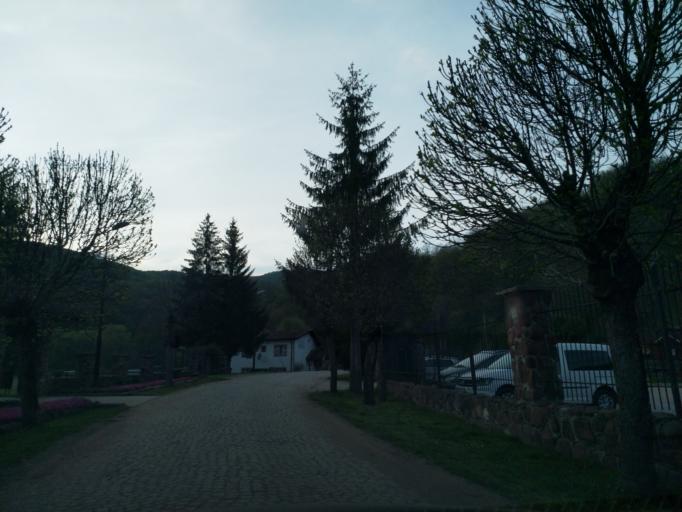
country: RS
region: Central Serbia
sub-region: Pomoravski Okrug
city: Despotovac
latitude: 43.9561
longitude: 21.5874
